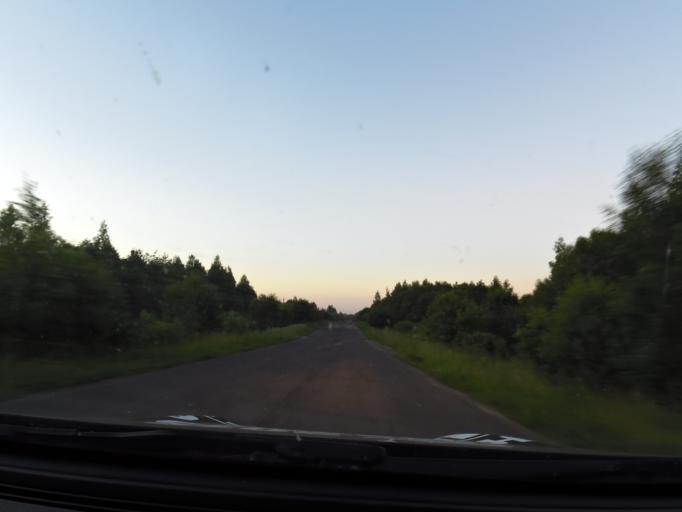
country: RU
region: Kostroma
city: Buy
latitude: 58.4105
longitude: 41.2457
